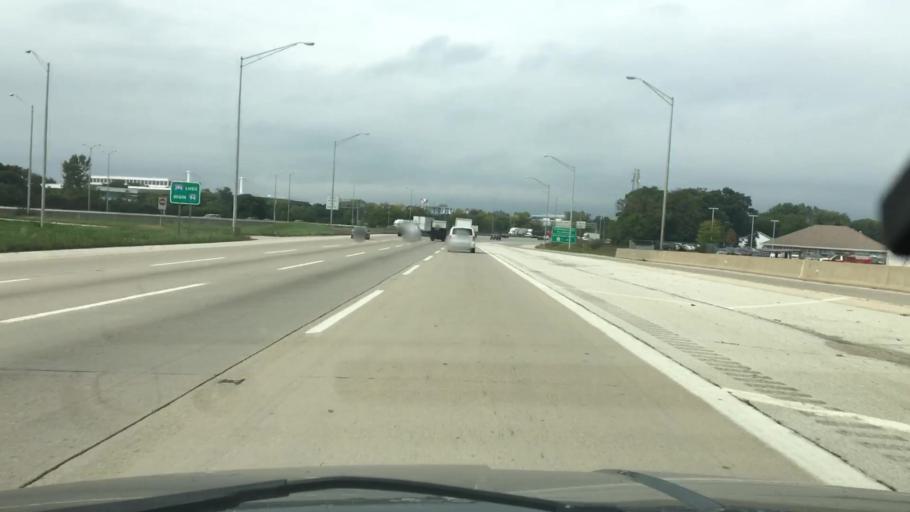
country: US
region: Illinois
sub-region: Lake County
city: Riverwoods
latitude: 42.1558
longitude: -87.8727
